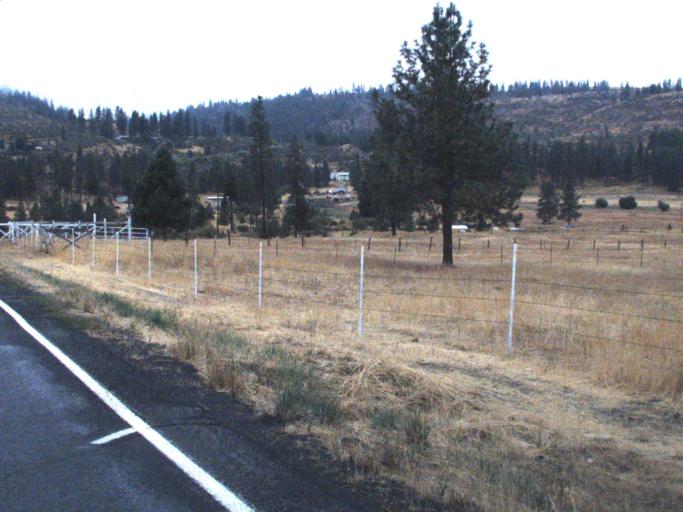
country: US
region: Washington
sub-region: Lincoln County
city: Davenport
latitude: 47.7849
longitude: -117.8892
